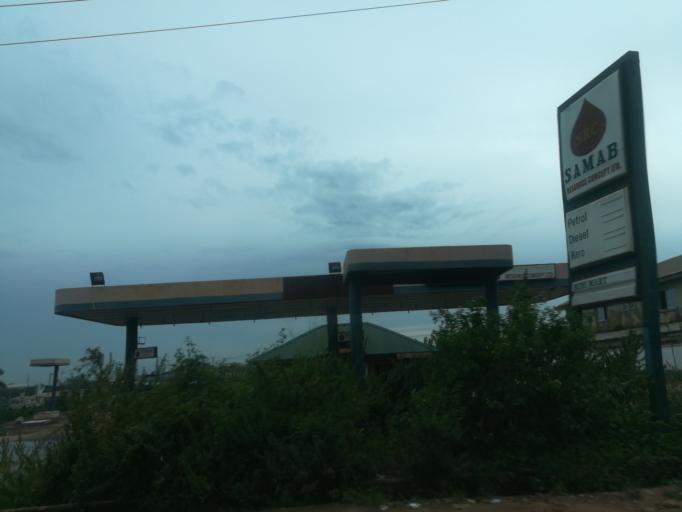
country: NG
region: Oyo
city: Egbeda
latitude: 7.3850
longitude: 3.9905
